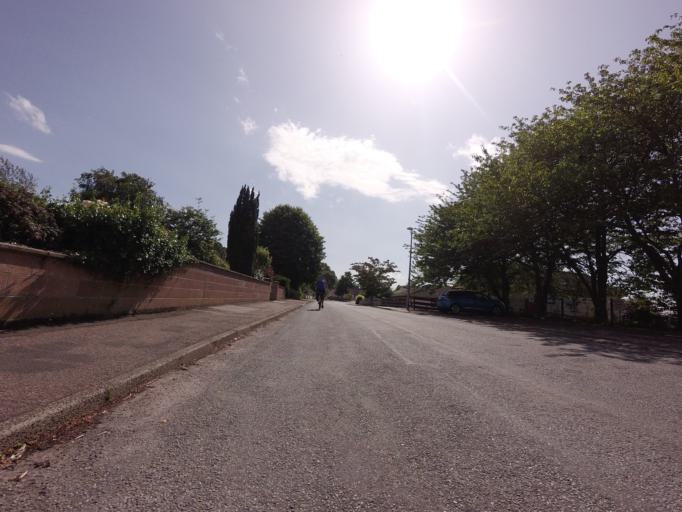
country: GB
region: Scotland
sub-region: Highland
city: Fortrose
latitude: 57.4966
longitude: -4.1210
